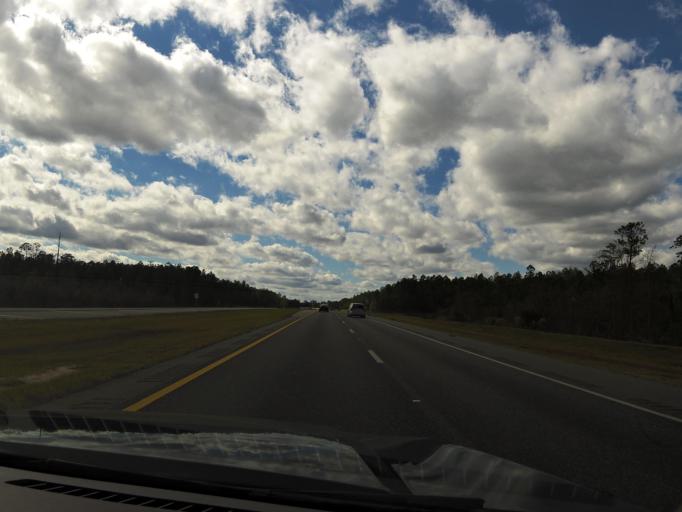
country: US
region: Florida
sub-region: Bradford County
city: Starke
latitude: 29.9903
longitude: -82.1007
